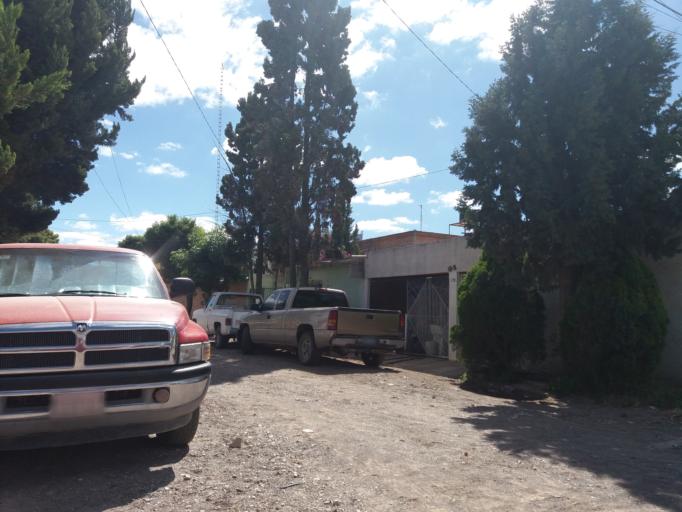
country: MX
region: Aguascalientes
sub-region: Aguascalientes
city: San Sebastian [Fraccionamiento]
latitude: 21.8023
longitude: -102.2761
